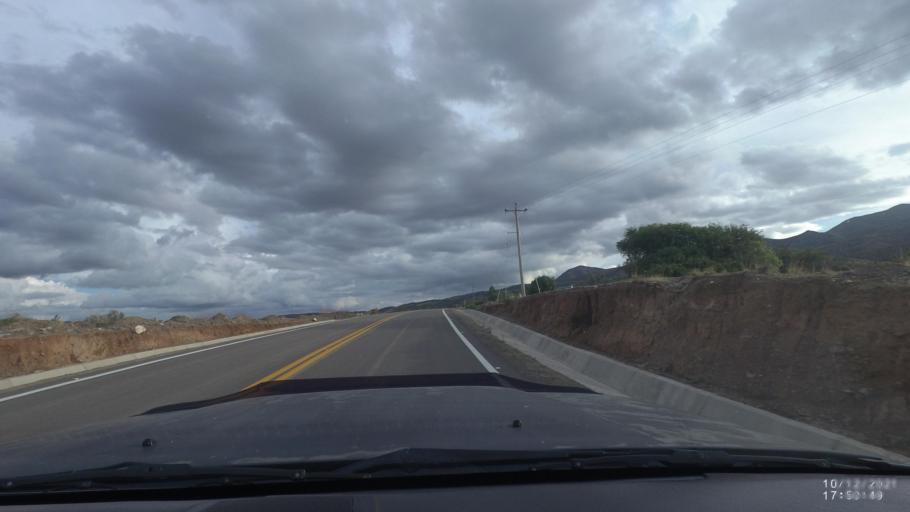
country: BO
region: Cochabamba
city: Tarata
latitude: -17.6703
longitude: -65.9617
